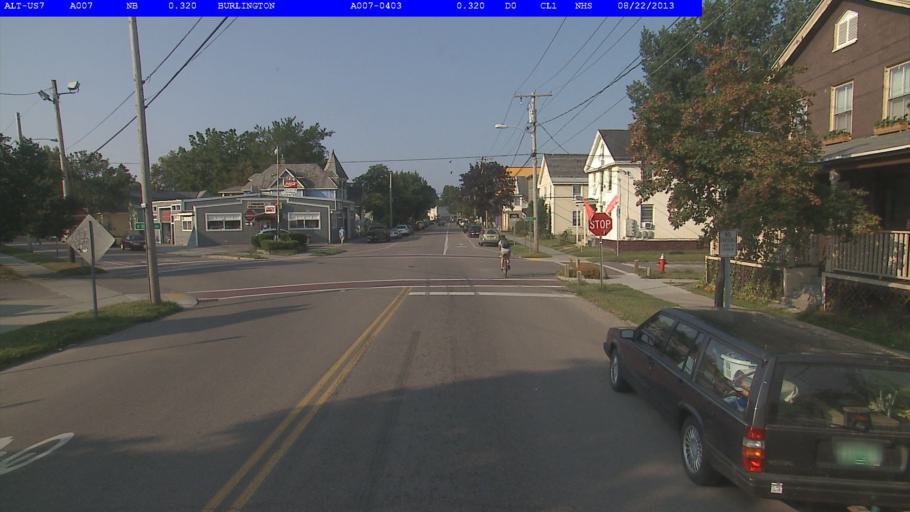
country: US
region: Vermont
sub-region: Chittenden County
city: Burlington
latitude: 44.4865
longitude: -73.2096
